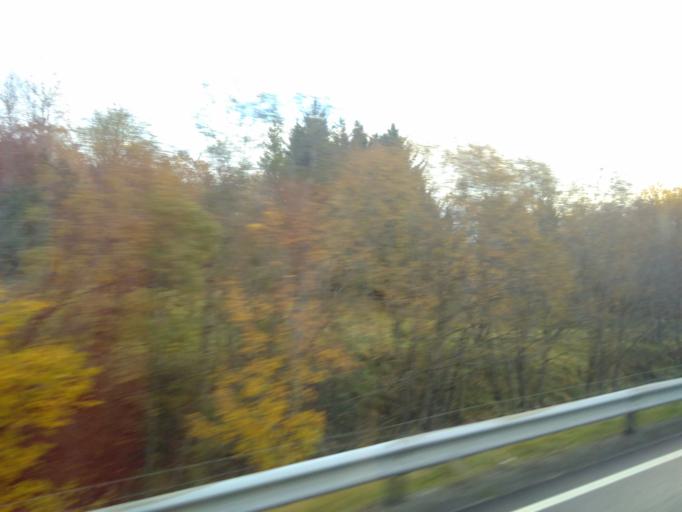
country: NO
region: Sor-Trondelag
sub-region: Hitra
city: Fillan
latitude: 63.5238
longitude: 9.0899
